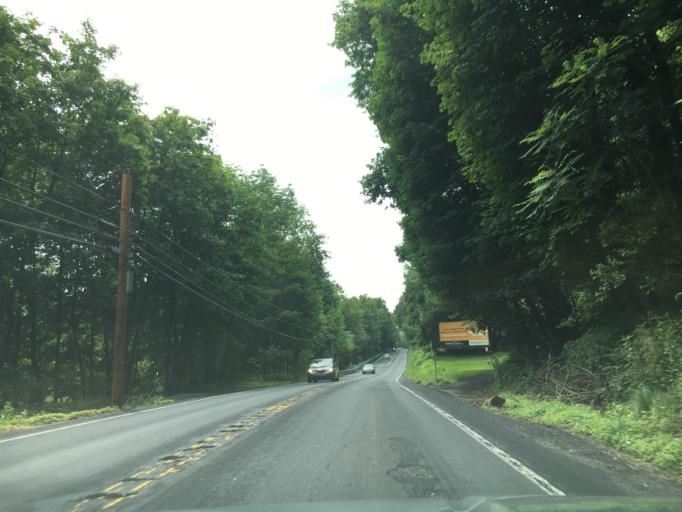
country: US
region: Pennsylvania
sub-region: Lehigh County
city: Laurys Station
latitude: 40.7197
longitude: -75.5269
